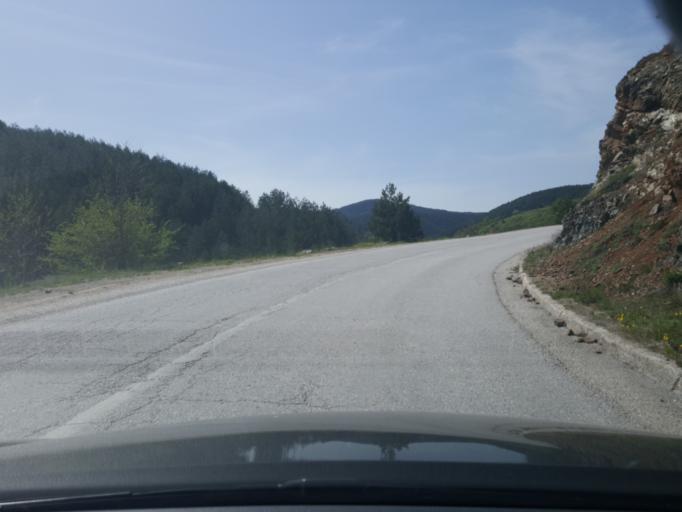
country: RS
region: Central Serbia
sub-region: Zlatiborski Okrug
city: Bajina Basta
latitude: 43.8605
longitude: 19.5796
